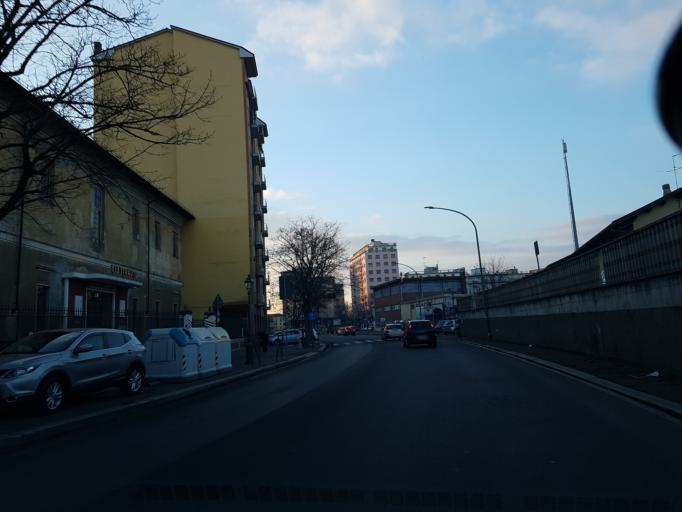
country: IT
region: Piedmont
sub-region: Provincia di Alessandria
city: Novi Ligure
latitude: 44.7615
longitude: 8.7885
